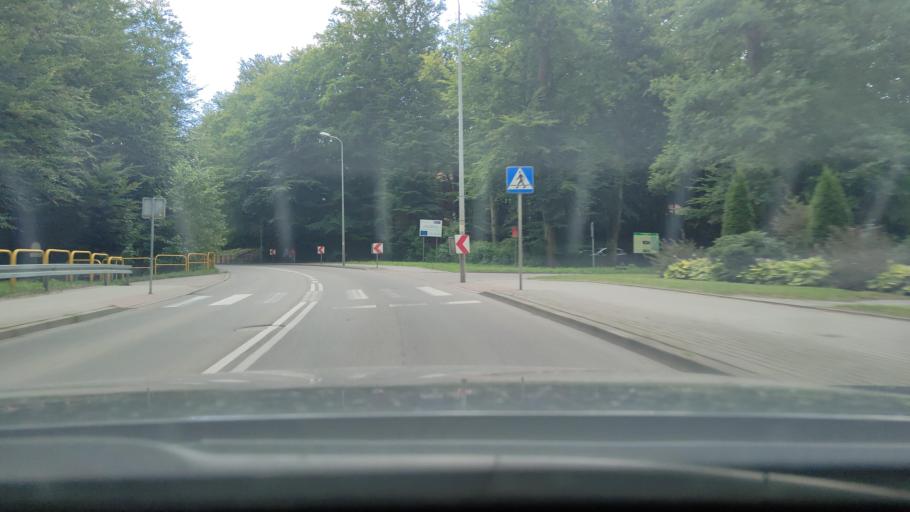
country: PL
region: Pomeranian Voivodeship
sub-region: Powiat wejherowski
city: Wejherowo
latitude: 54.5956
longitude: 18.2328
